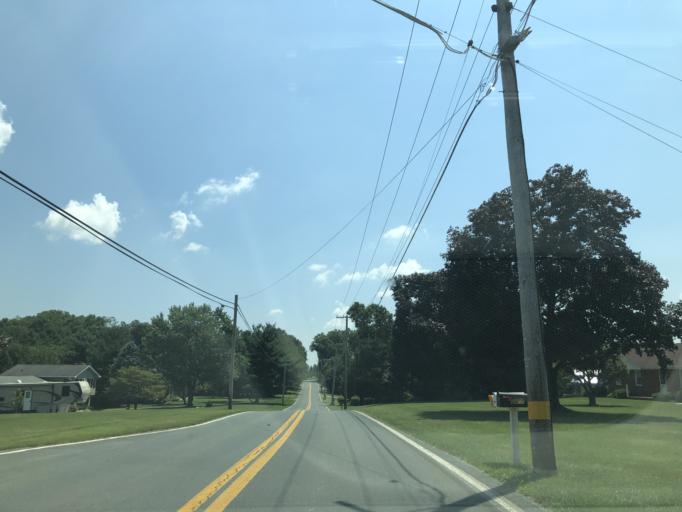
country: US
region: Maryland
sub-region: Carroll County
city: Westminster
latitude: 39.5386
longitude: -76.9766
